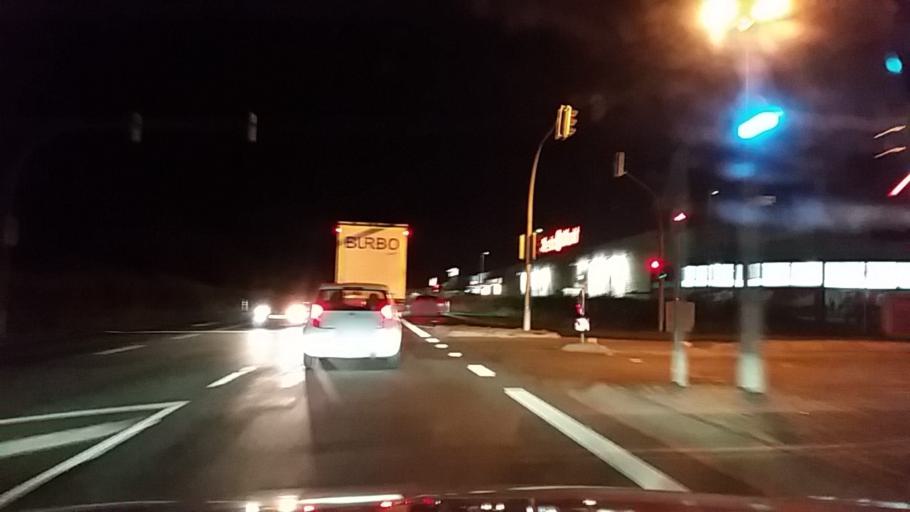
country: DE
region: Lower Saxony
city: Lehre
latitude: 52.3685
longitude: 10.7318
